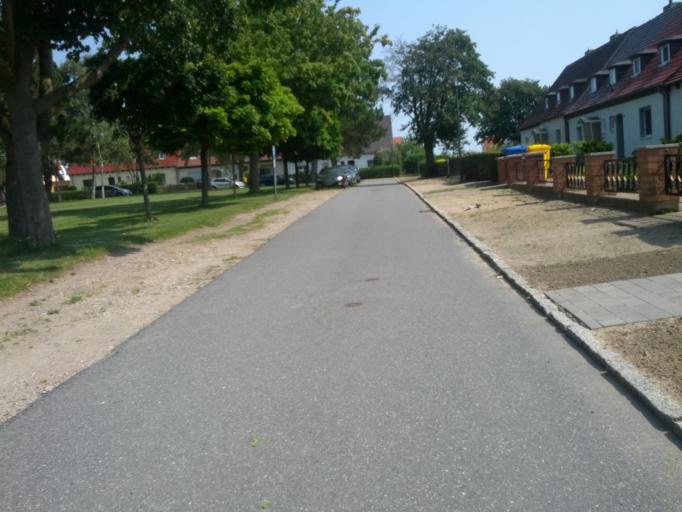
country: DE
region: Mecklenburg-Vorpommern
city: Bastorf
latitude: 54.1035
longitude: 11.6189
